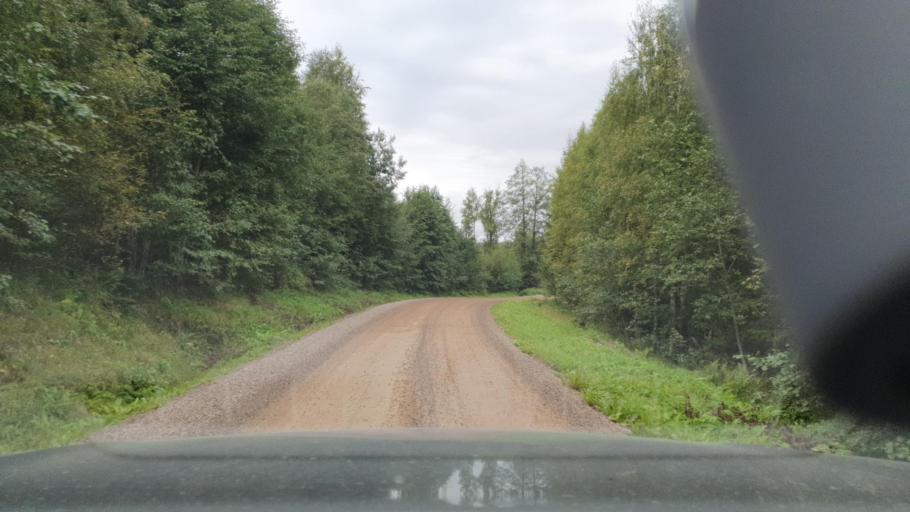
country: SE
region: Vaermland
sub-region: Arvika Kommun
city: Arvika
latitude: 60.0038
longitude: 12.6596
